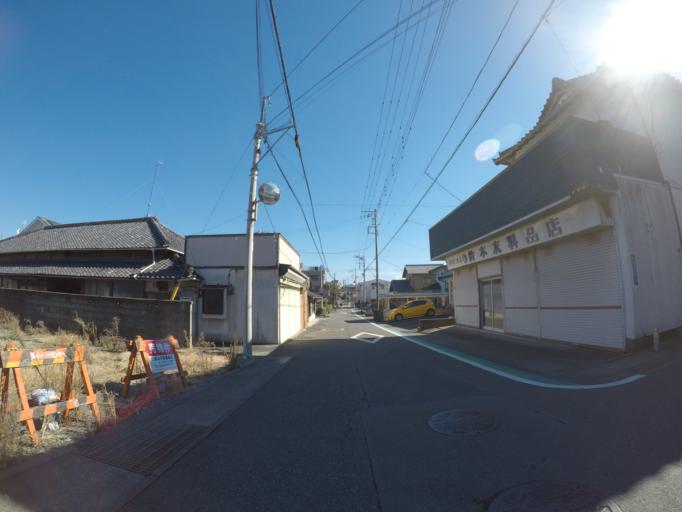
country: JP
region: Shizuoka
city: Fuji
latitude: 35.1672
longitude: 138.6959
